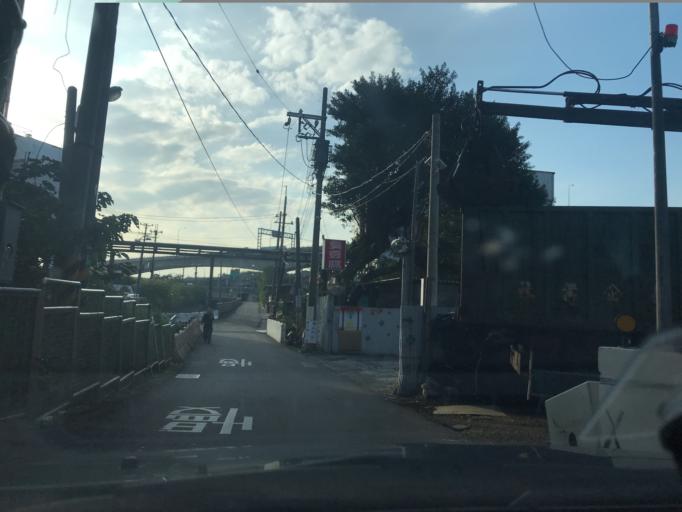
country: TW
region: Taiwan
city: Taoyuan City
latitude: 24.9860
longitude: 121.2372
